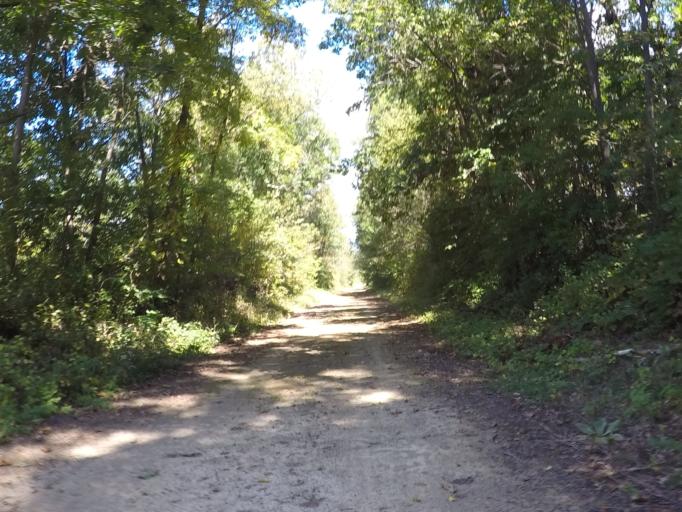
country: US
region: Wisconsin
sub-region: Richland County
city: Richland Center
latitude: 43.2269
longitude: -90.2981
